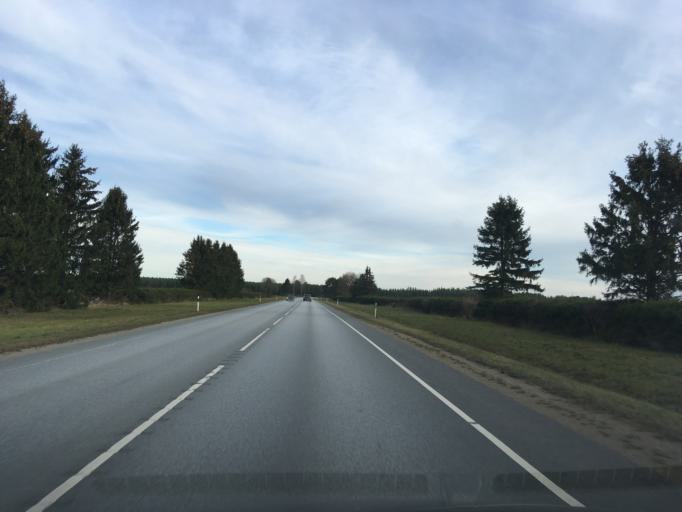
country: EE
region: Laeaene-Virumaa
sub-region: Viru-Nigula vald
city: Kunda
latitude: 59.3869
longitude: 26.6150
